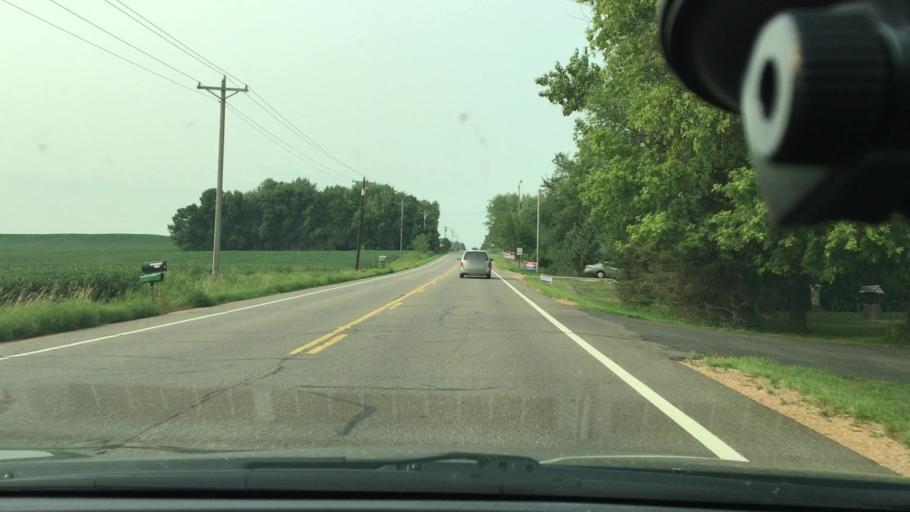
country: US
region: Minnesota
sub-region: Hennepin County
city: Champlin
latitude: 45.1596
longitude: -93.4620
